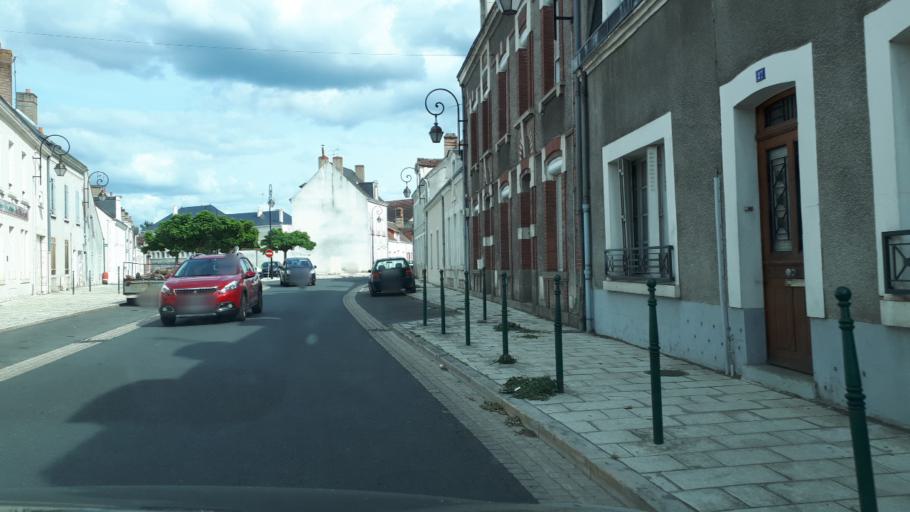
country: FR
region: Centre
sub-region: Departement du Loir-et-Cher
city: Romorantin-Lanthenay
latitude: 47.3540
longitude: 1.7432
